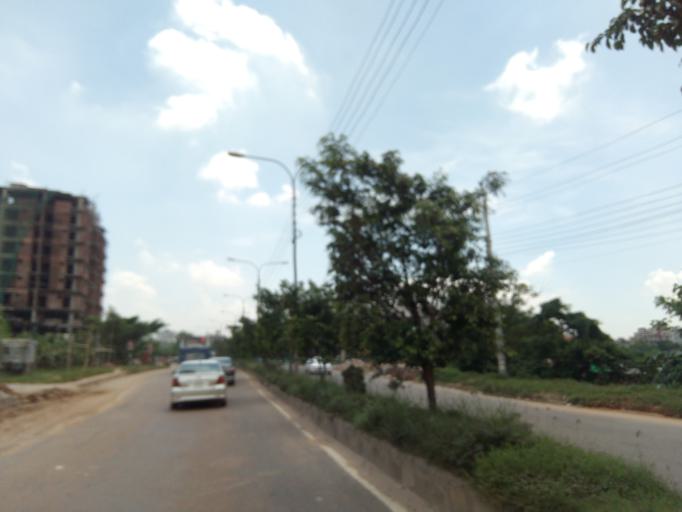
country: BD
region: Dhaka
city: Tungi
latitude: 23.8202
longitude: 90.3872
